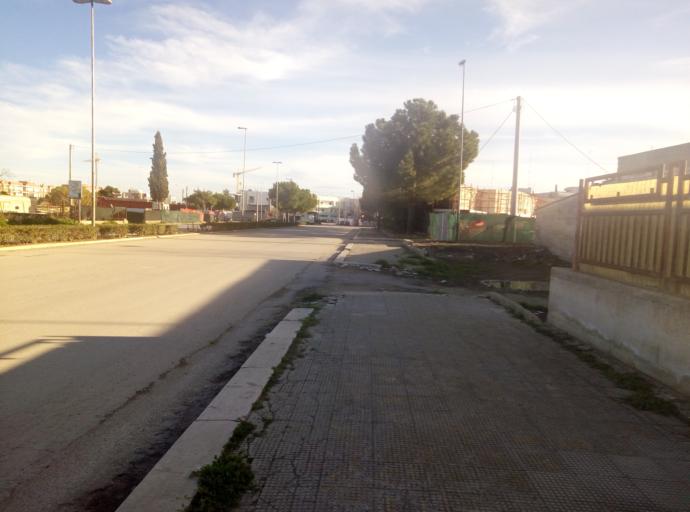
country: IT
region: Apulia
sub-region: Provincia di Bari
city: Ruvo di Puglia
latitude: 41.1180
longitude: 16.4921
